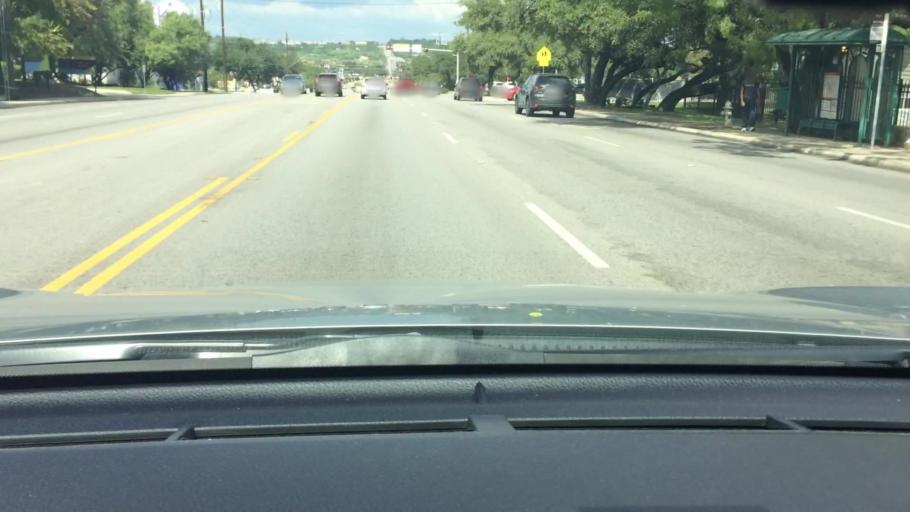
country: US
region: Texas
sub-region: Bexar County
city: Shavano Park
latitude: 29.5496
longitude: -98.5736
